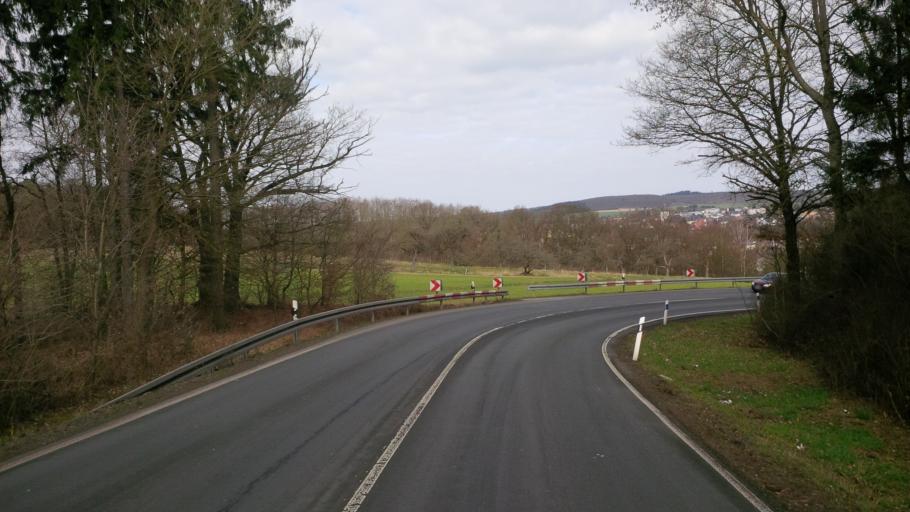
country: DE
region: Hesse
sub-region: Regierungsbezirk Darmstadt
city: Usingen
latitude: 50.3243
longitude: 8.5464
